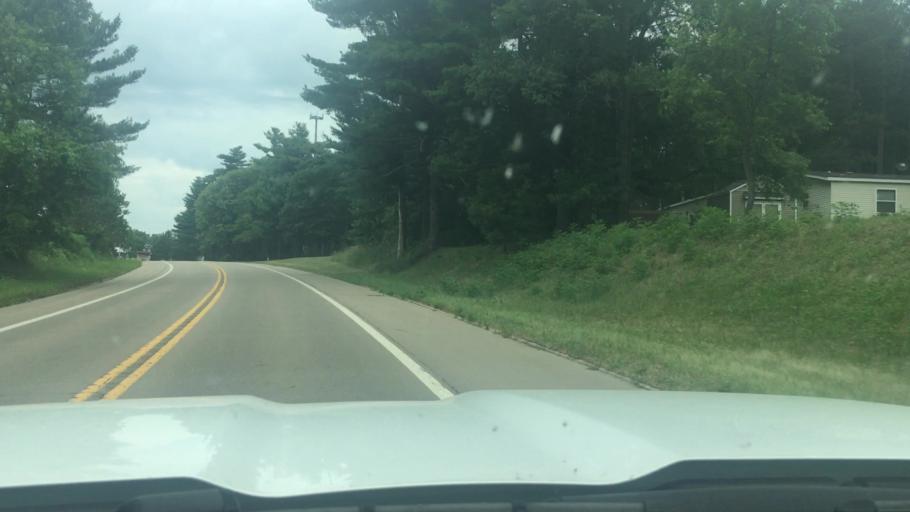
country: US
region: Michigan
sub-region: Clinton County
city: Fowler
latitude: 42.9998
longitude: -84.8694
